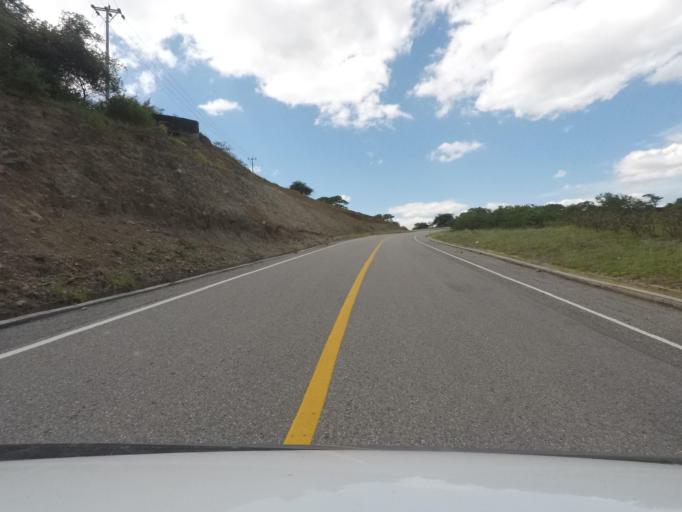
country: TL
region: Lautem
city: Lospalos
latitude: -8.4041
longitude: 126.8180
